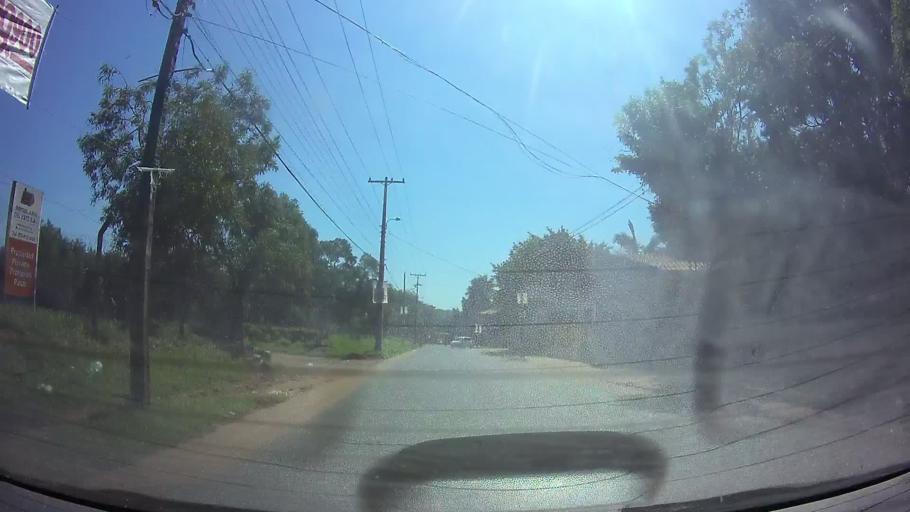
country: PY
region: Central
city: Fernando de la Mora
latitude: -25.3192
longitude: -57.5220
